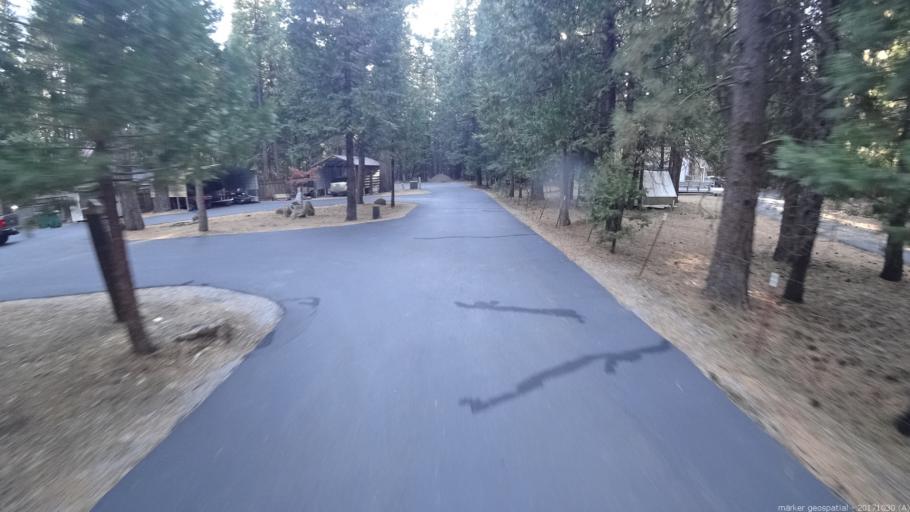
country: US
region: California
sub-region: Shasta County
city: Shingletown
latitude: 40.5583
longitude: -121.7242
